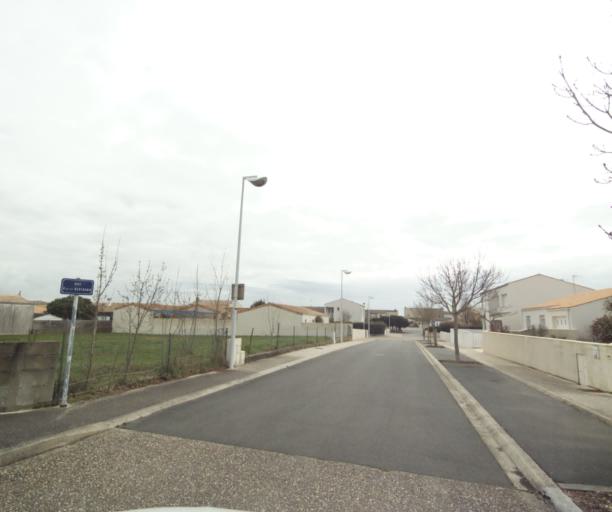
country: FR
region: Poitou-Charentes
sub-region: Departement de la Charente-Maritime
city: Lagord
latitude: 46.1867
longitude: -1.1646
